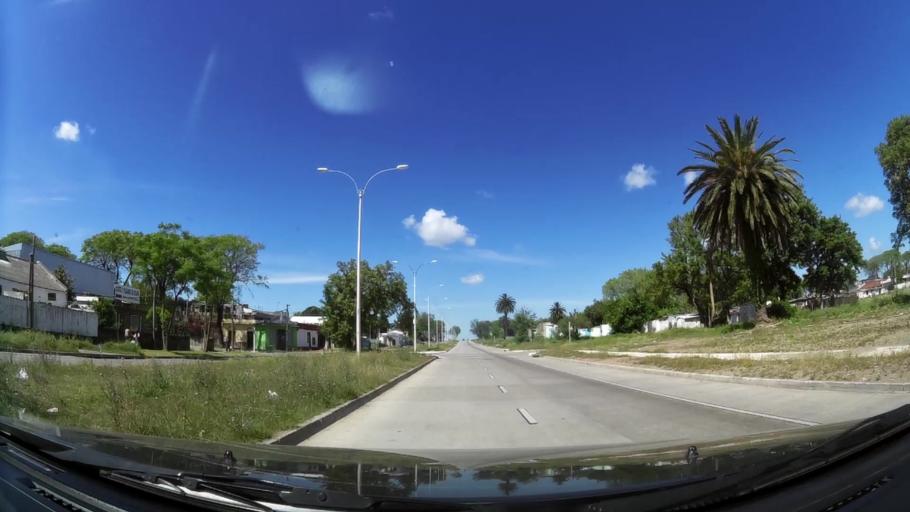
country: UY
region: Montevideo
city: Montevideo
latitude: -34.8437
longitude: -56.1435
